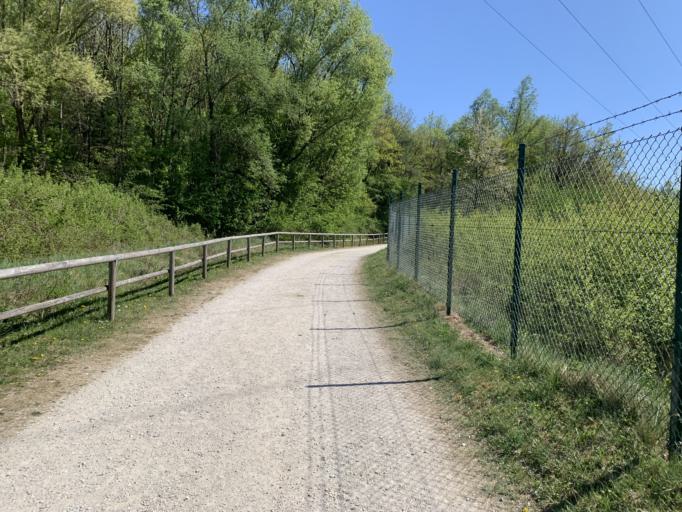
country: DE
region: Bavaria
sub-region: Swabia
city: Gersthofen
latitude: 48.4218
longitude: 10.8917
